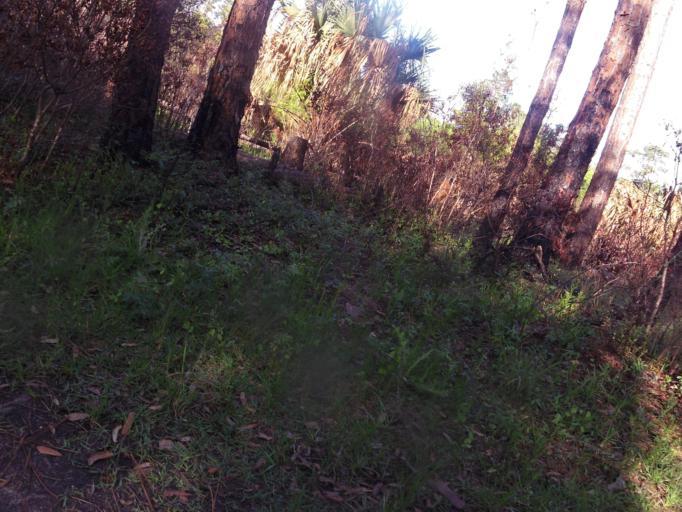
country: US
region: Florida
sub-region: Saint Johns County
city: Villano Beach
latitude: 30.0248
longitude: -81.3389
